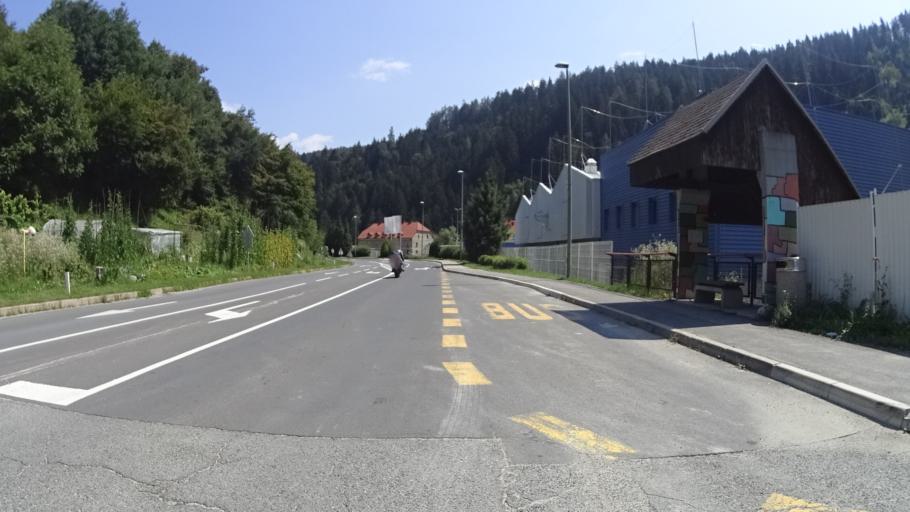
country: SI
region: Prevalje
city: Prevalje
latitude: 46.5421
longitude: 14.9052
